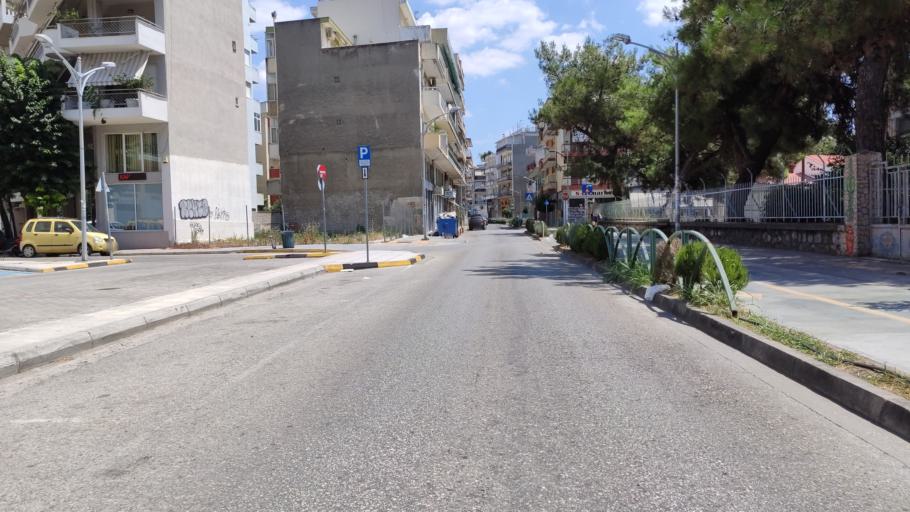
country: GR
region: East Macedonia and Thrace
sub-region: Nomos Rodopis
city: Komotini
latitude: 41.1154
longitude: 25.3999
